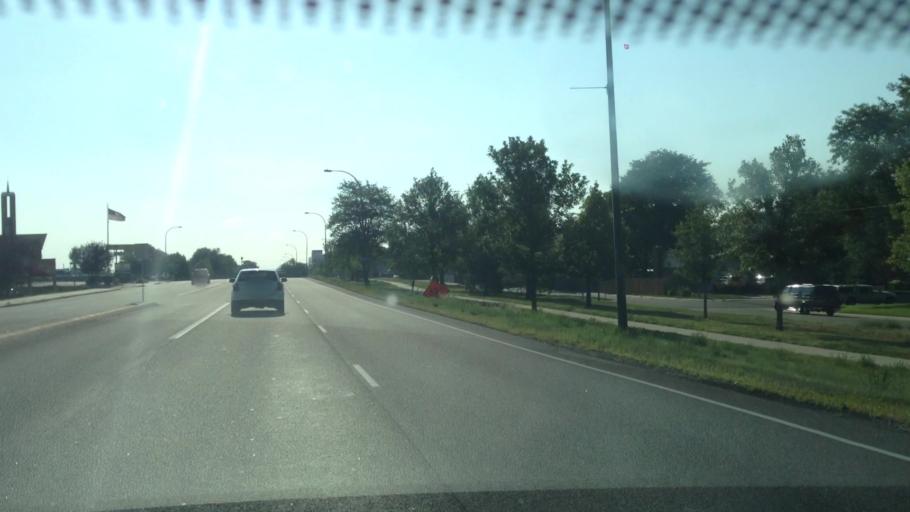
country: US
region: Colorado
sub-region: Jefferson County
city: Lakewood
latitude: 39.7110
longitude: -105.0698
